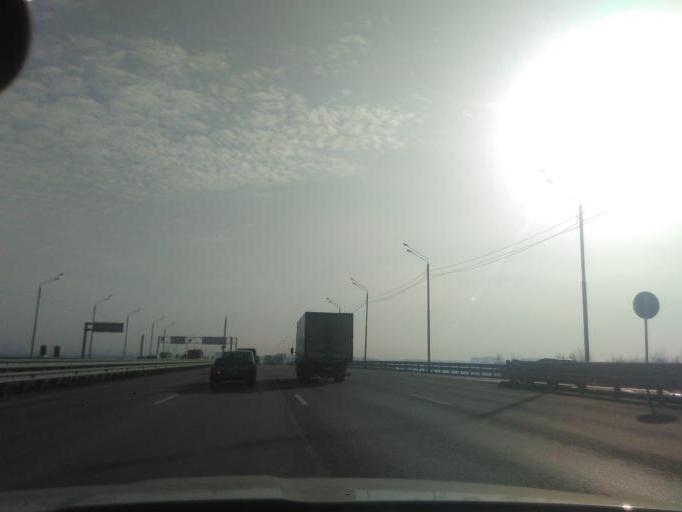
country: RU
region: Moskovskaya
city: Krasnogorsk
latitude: 55.8009
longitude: 37.3282
